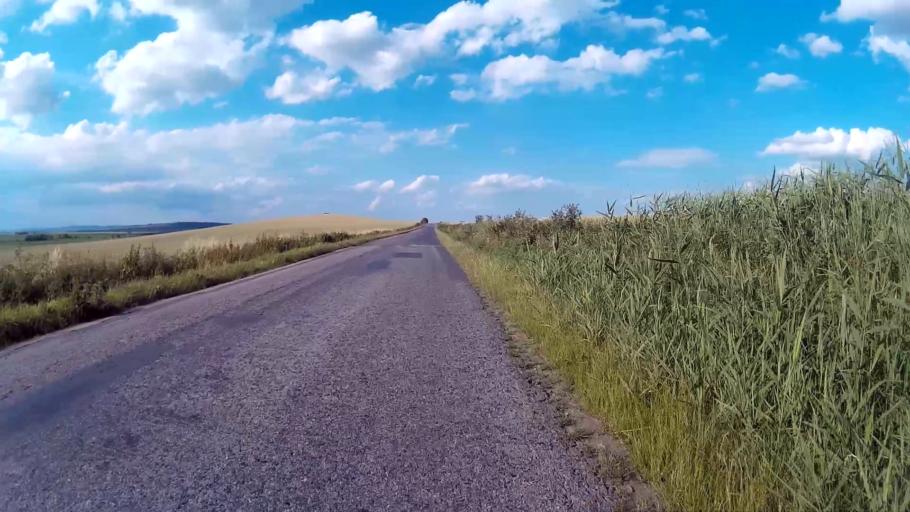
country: CZ
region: South Moravian
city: Tesany
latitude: 49.0555
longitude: 16.7786
